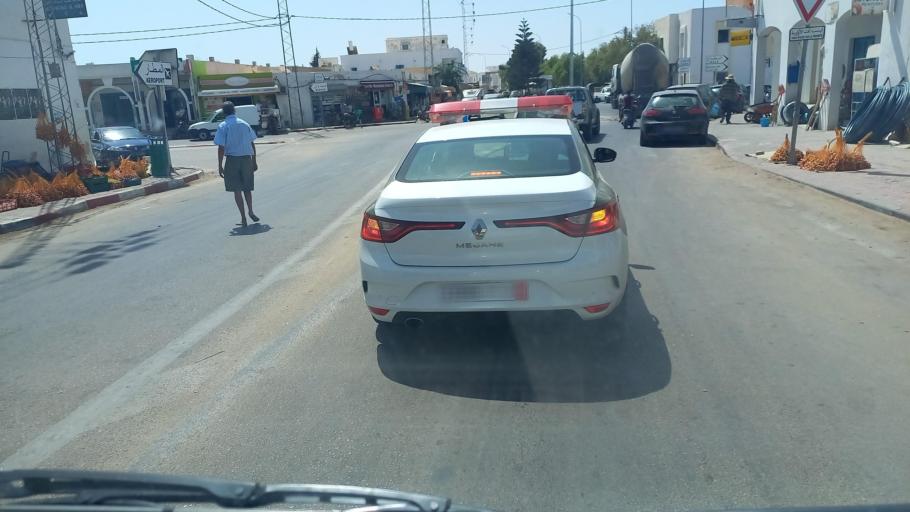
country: TN
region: Madanin
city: Houmt Souk
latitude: 33.8016
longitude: 10.8832
